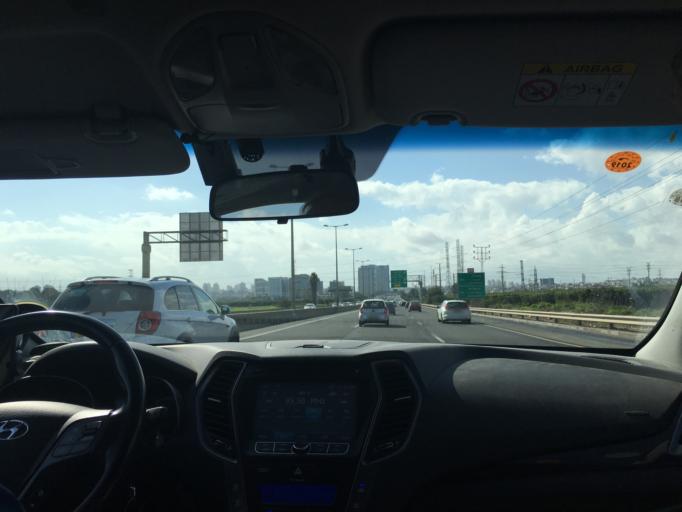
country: IL
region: Tel Aviv
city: Ramat HaSharon
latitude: 32.1133
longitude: 34.8506
